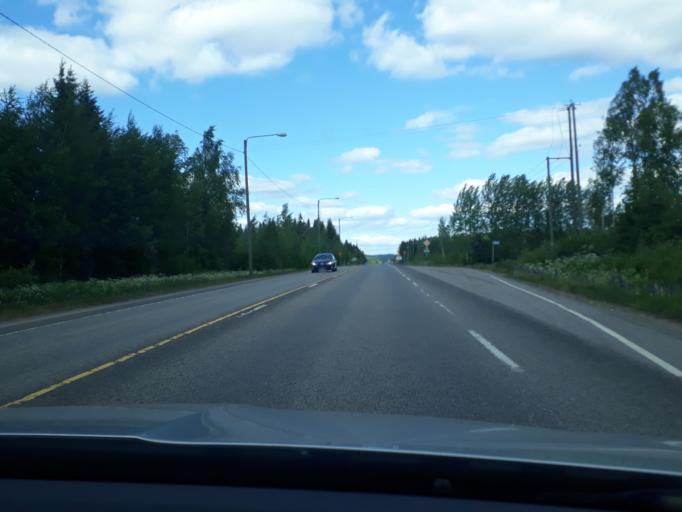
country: FI
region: Central Finland
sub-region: AEaenekoski
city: AEaenekoski
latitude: 62.6460
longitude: 25.7092
